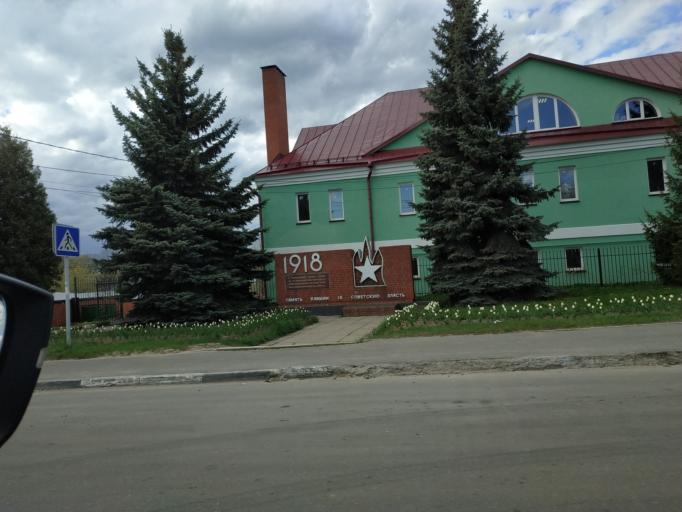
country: RU
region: Moskovskaya
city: Pavlovskiy Posad
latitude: 55.7812
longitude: 38.6502
